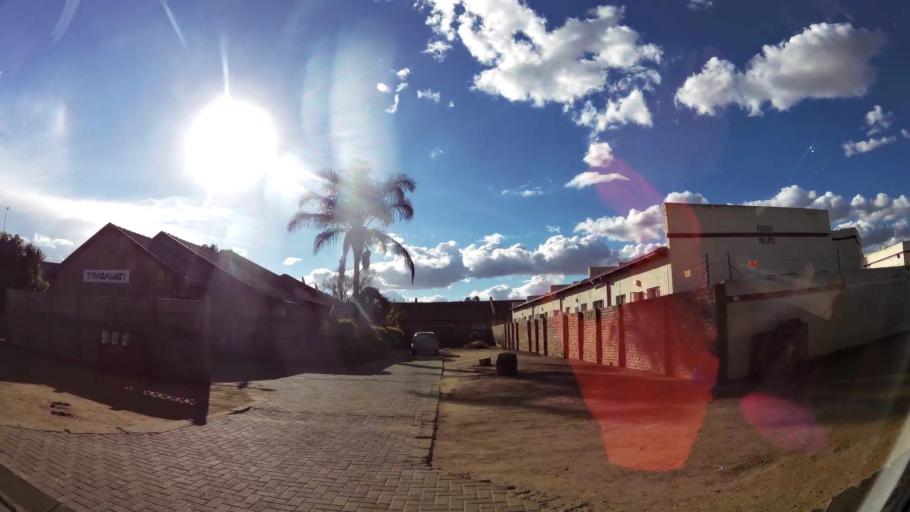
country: ZA
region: Limpopo
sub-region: Capricorn District Municipality
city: Polokwane
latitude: -23.9325
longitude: 29.4522
